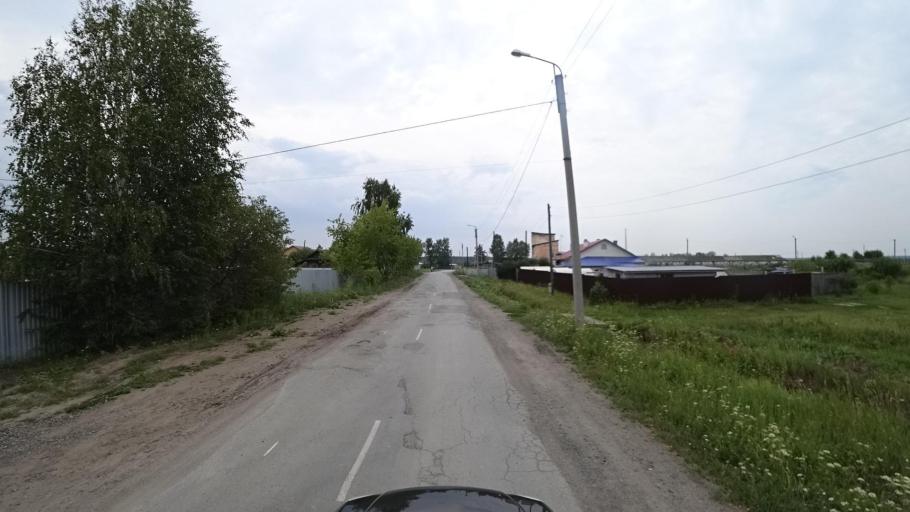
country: RU
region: Sverdlovsk
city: Kamyshlov
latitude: 56.8480
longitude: 62.7356
